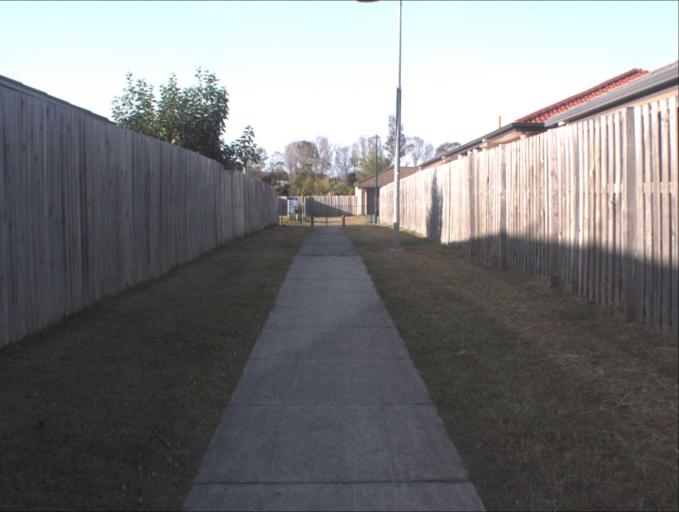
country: AU
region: Queensland
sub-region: Logan
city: Beenleigh
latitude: -27.6853
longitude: 153.1743
